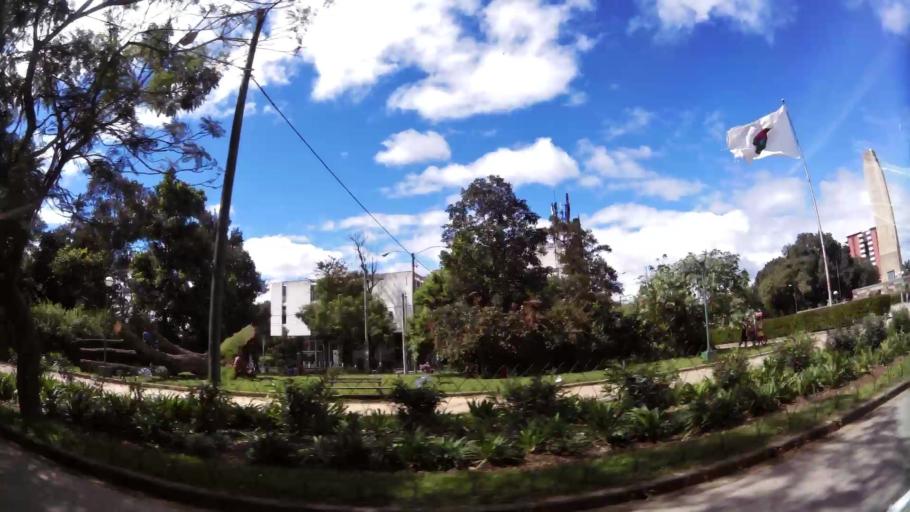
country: GT
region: Guatemala
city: Santa Catarina Pinula
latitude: 14.5935
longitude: -90.5178
